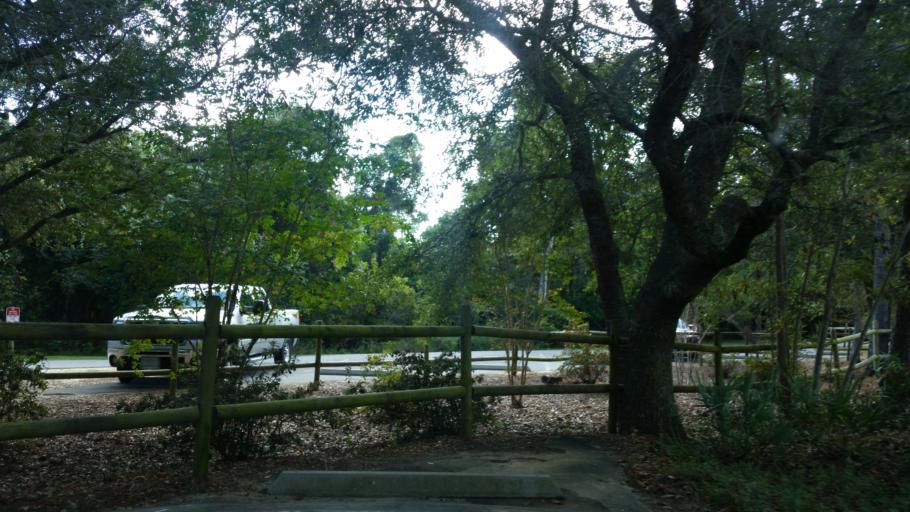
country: US
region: Alabama
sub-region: Baldwin County
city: Orange Beach
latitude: 30.2805
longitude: -87.5818
